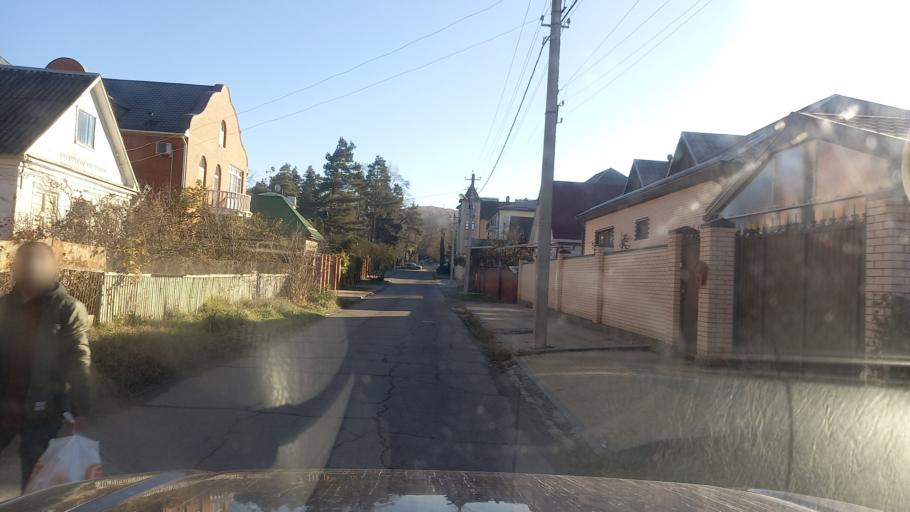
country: RU
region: Krasnodarskiy
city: Goryachiy Klyuch
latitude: 44.6282
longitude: 39.1047
